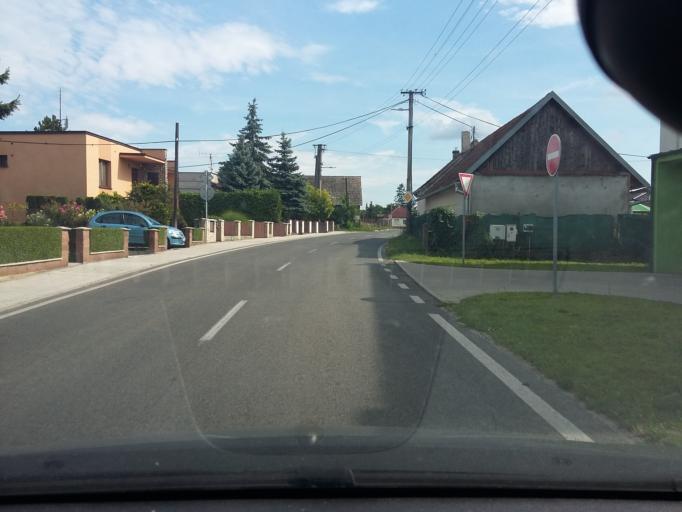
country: SK
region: Trnavsky
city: Gbely
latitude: 48.6312
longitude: 17.2063
